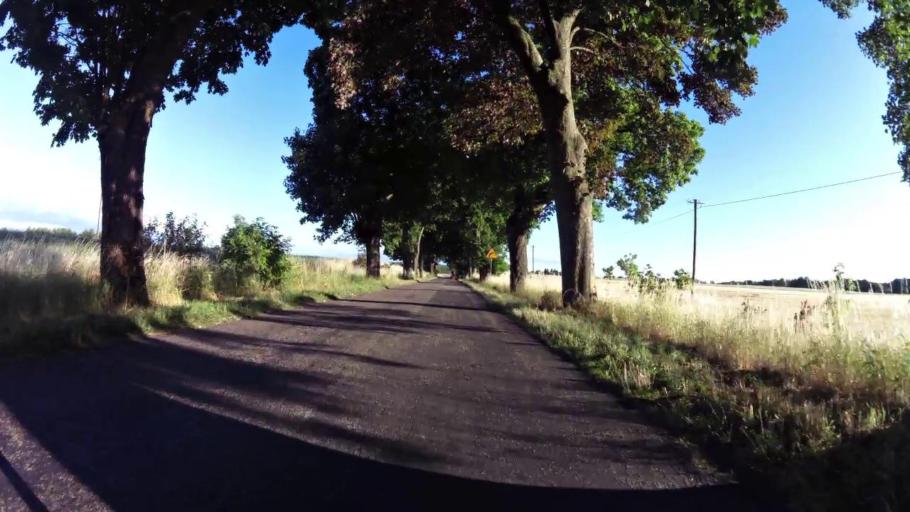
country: PL
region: West Pomeranian Voivodeship
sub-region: Powiat swidwinski
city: Swidwin
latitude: 53.7498
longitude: 15.6897
